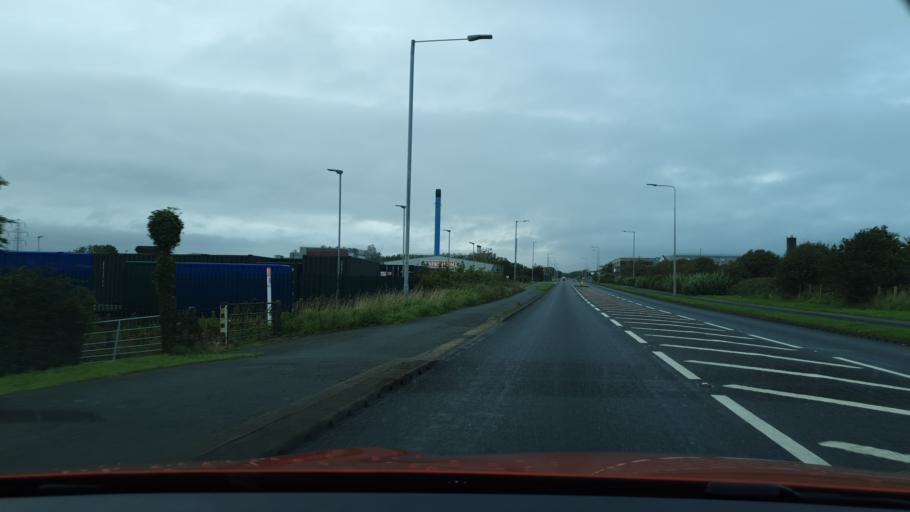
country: GB
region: England
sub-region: Cumbria
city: Barrow in Furness
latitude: 54.1390
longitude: -3.2332
